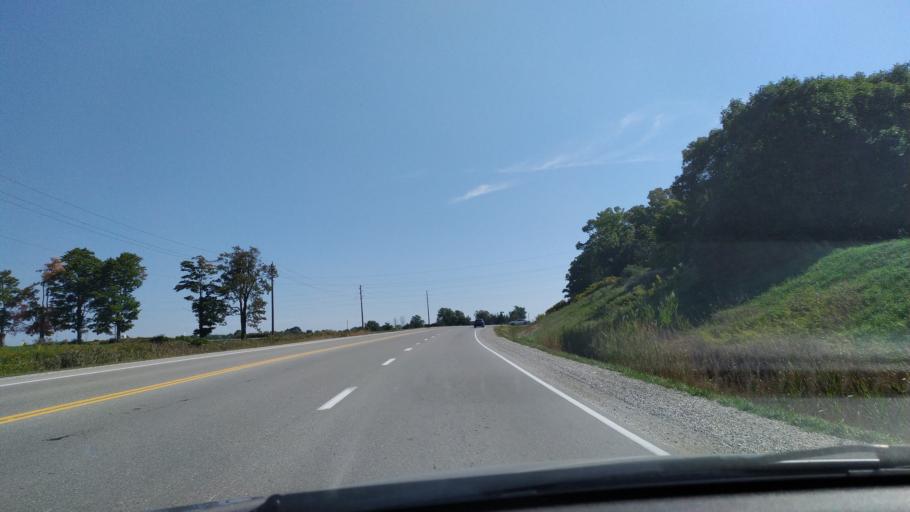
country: CA
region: Ontario
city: Ingersoll
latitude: 43.0649
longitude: -80.8404
